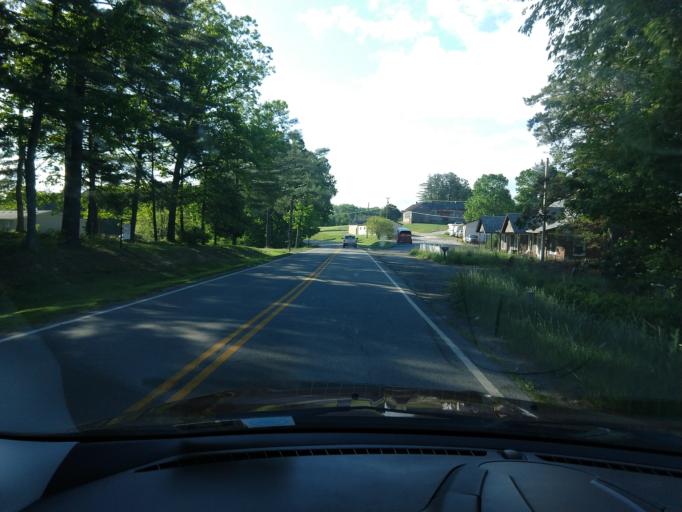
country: US
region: Virginia
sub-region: City of Galax
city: Galax
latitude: 36.7427
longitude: -80.9822
